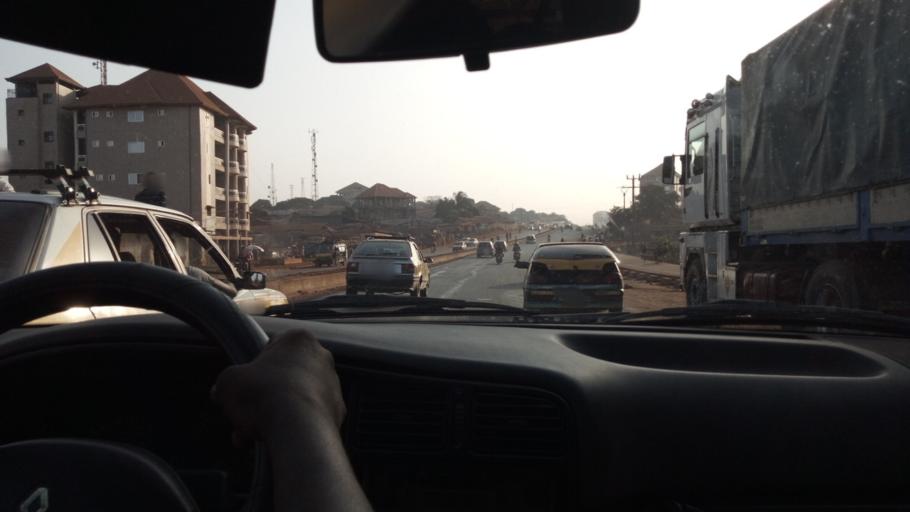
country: GN
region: Kindia
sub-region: Prefecture de Dubreka
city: Dubreka
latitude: 9.6779
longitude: -13.5426
